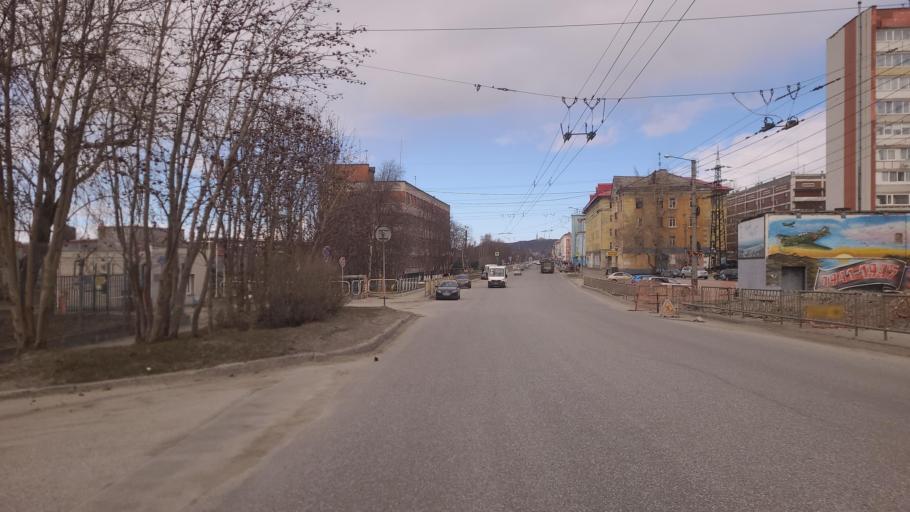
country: RU
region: Murmansk
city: Murmansk
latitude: 68.9576
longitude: 33.0628
